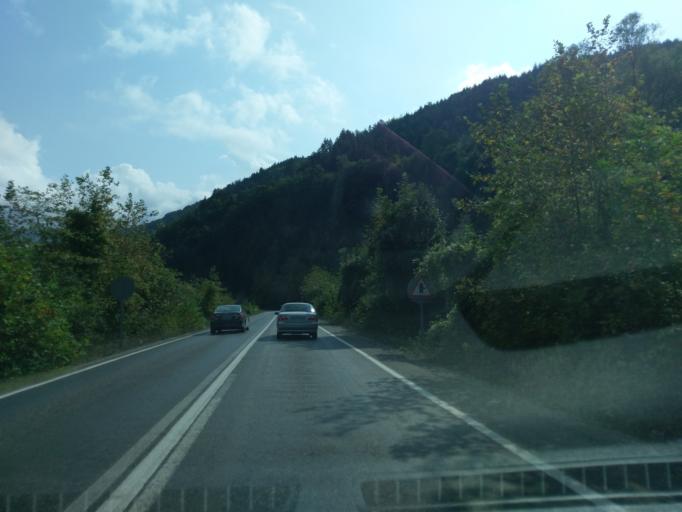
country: TR
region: Sinop
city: Yenikonak
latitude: 41.8778
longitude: 34.5521
